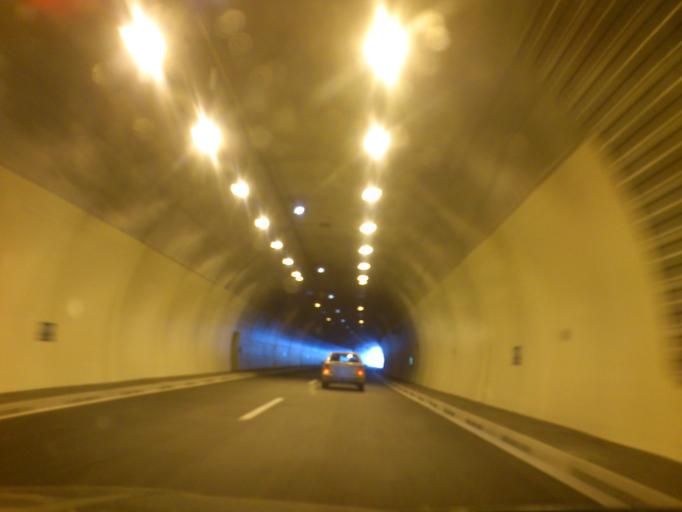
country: AT
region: Upper Austria
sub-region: Politischer Bezirk Freistadt
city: Freistadt
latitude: 48.4968
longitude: 14.5164
